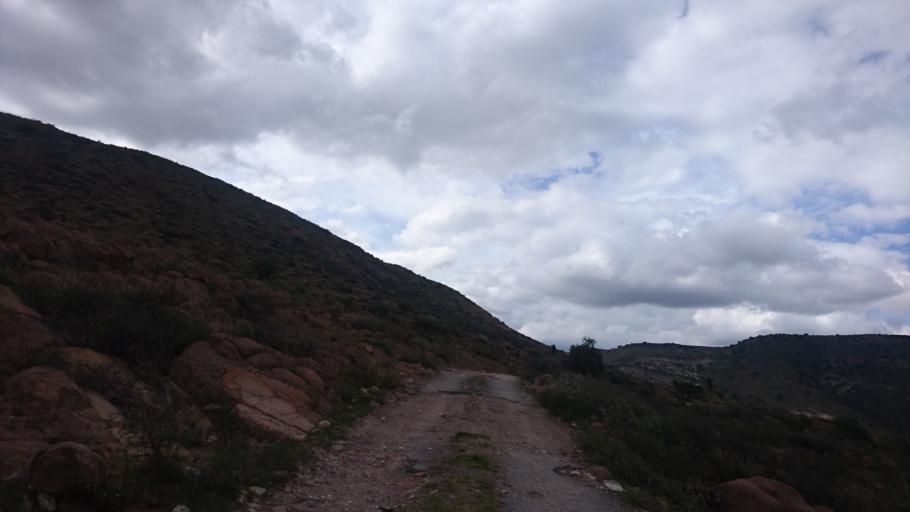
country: MX
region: San Luis Potosi
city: Escalerillas
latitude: 22.0835
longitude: -101.1011
